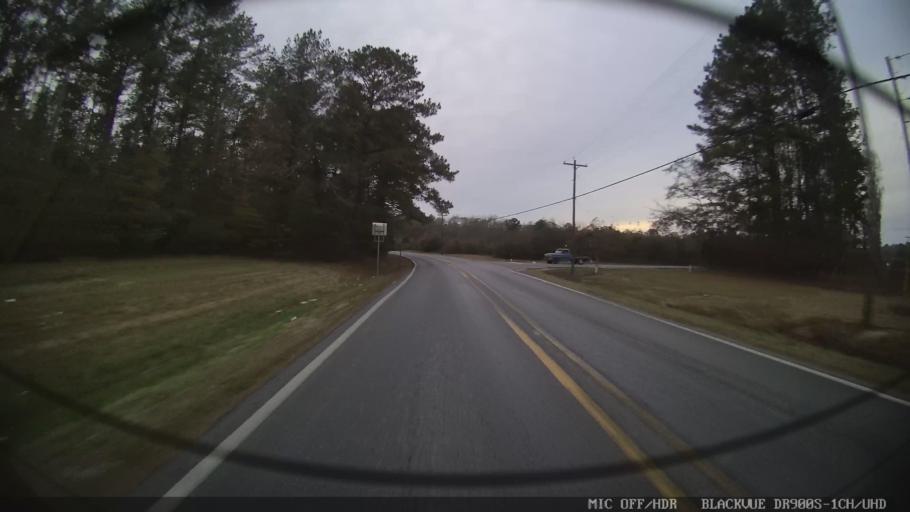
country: US
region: Mississippi
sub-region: Clarke County
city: Quitman
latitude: 32.0427
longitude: -88.7521
